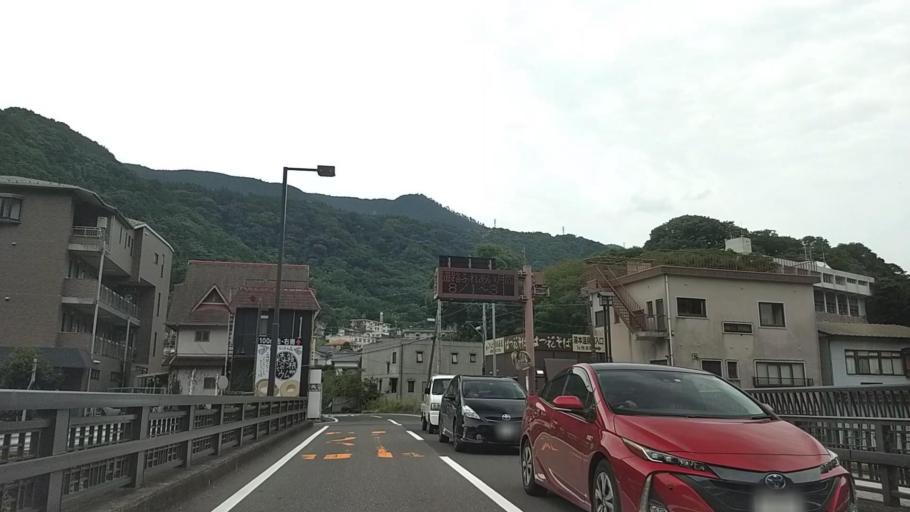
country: JP
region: Kanagawa
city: Odawara
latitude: 35.2336
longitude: 139.1087
